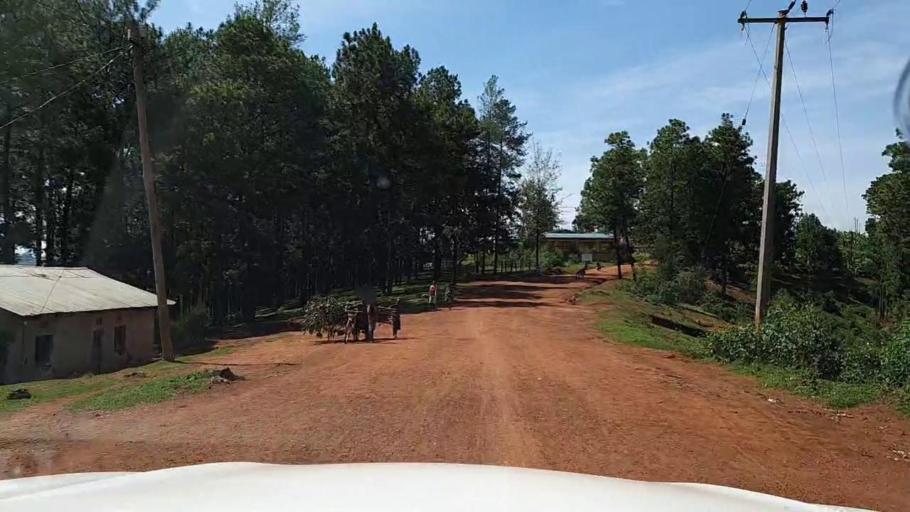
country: RW
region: Southern Province
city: Butare
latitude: -2.7161
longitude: 29.8394
